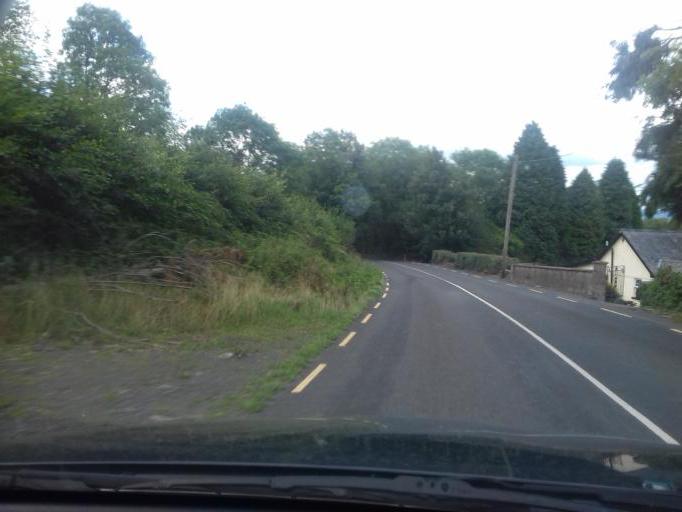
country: IE
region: Leinster
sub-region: Kilkenny
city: Graiguenamanagh
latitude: 52.5050
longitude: -6.9475
